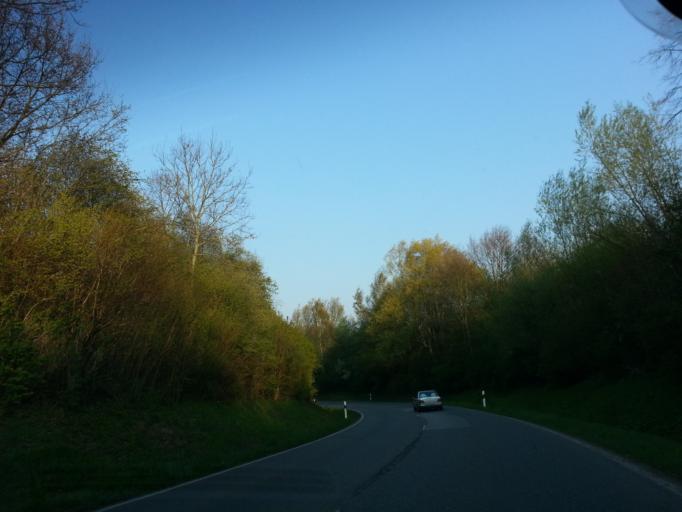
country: DE
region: Schleswig-Holstein
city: Scharbeutz
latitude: 54.0214
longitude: 10.7529
